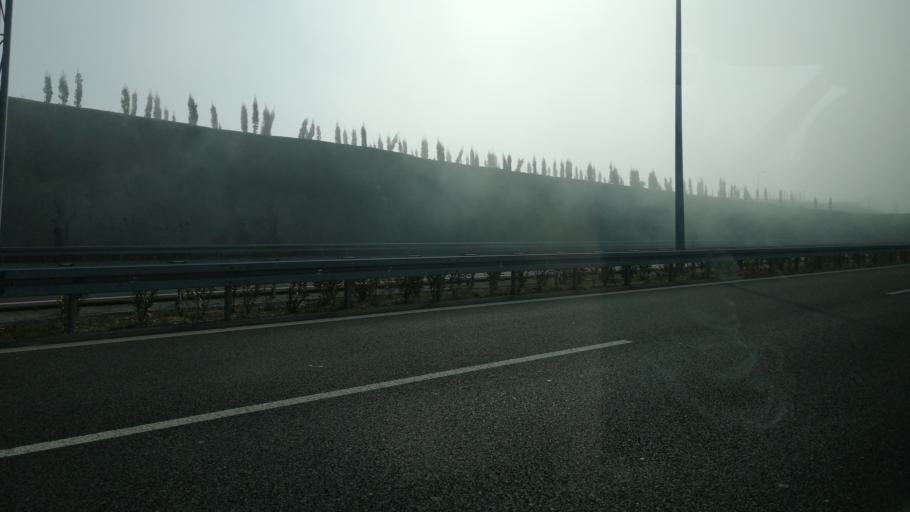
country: TR
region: Kocaeli
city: Tavsanli
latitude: 40.7761
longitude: 29.5183
